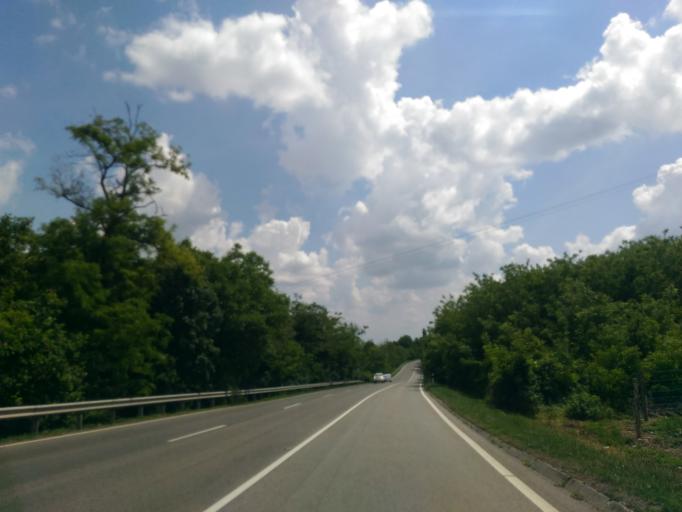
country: HU
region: Baranya
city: Pecs
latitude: 46.1252
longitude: 18.2591
